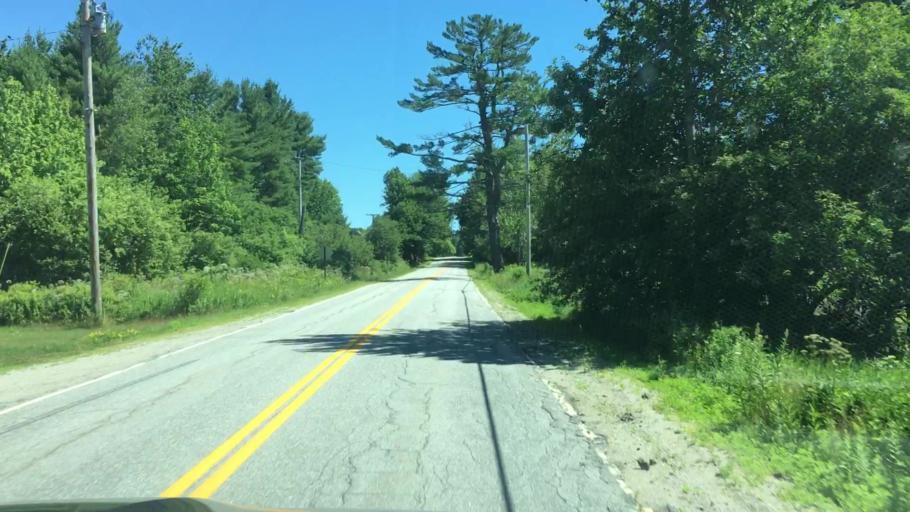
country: US
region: Maine
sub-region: Hancock County
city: Penobscot
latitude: 44.5177
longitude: -68.6686
